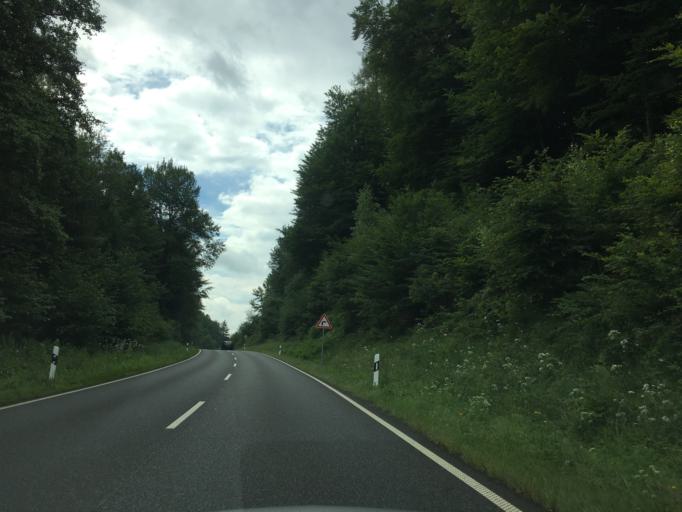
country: DE
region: Hesse
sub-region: Regierungsbezirk Darmstadt
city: Wachtersbach
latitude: 50.2879
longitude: 9.3034
